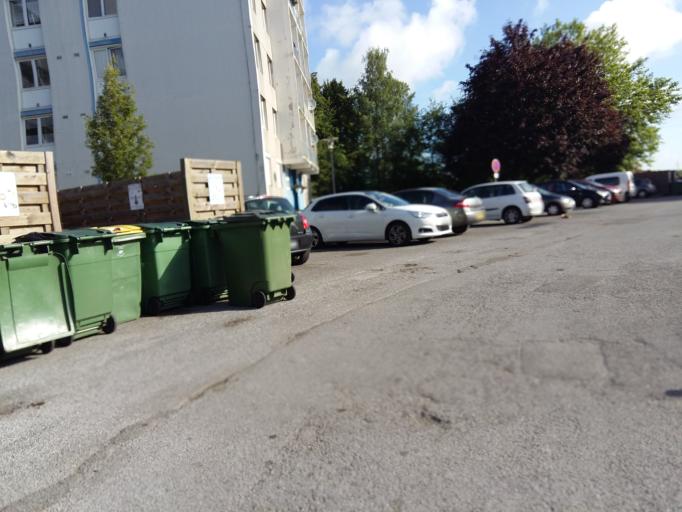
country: FR
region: Picardie
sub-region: Departement de la Somme
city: Rivery
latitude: 49.9143
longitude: 2.3236
